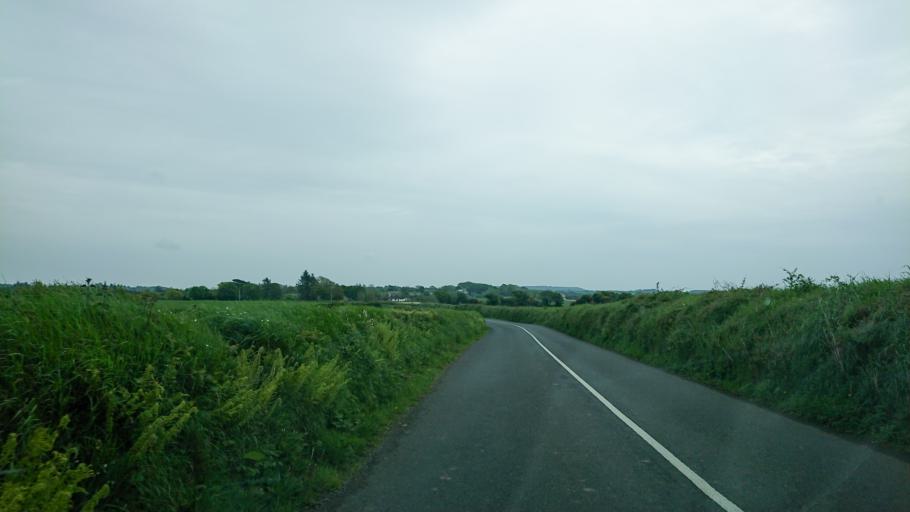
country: IE
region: Munster
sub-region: Waterford
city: Waterford
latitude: 52.2198
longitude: -7.0485
